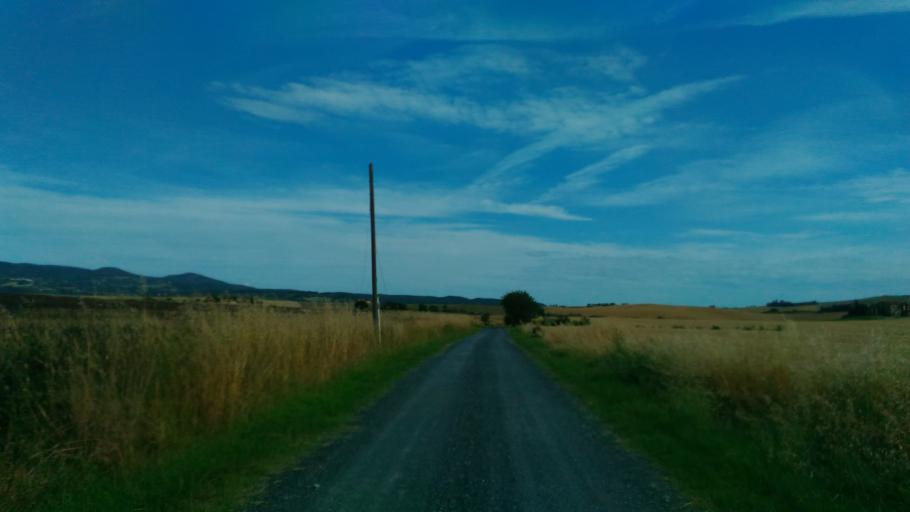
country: IT
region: Tuscany
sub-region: Province of Pisa
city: Orciano Pisano
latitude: 43.4474
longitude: 10.5202
